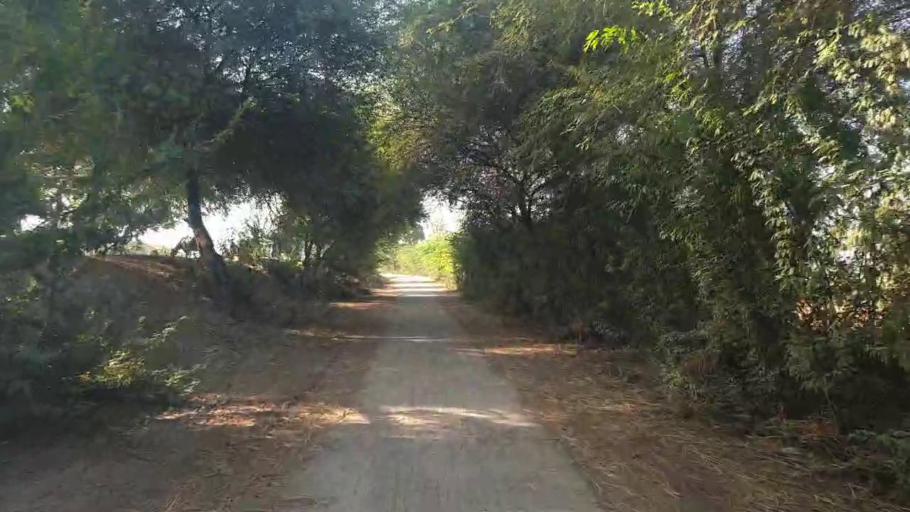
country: PK
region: Sindh
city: Tando Bago
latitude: 24.7429
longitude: 68.9310
